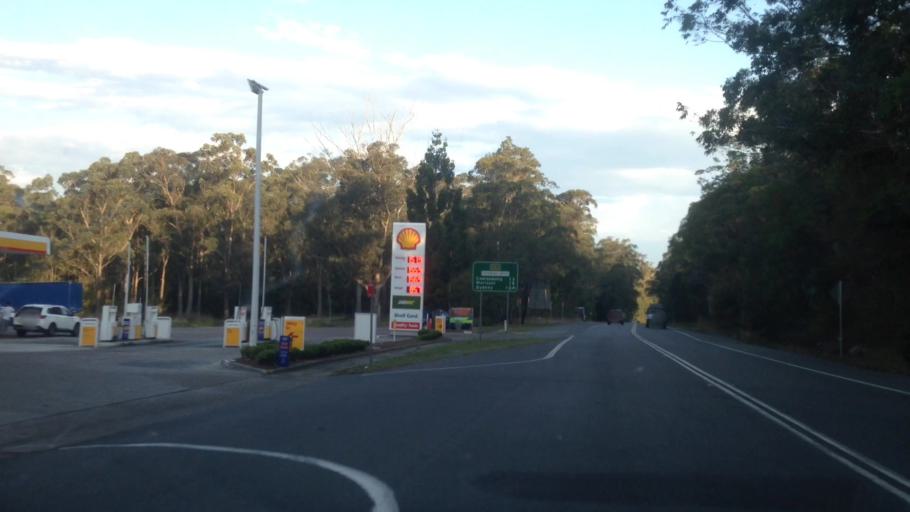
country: AU
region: New South Wales
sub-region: Lake Macquarie Shire
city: Cooranbong
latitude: -32.9856
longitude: 151.4866
